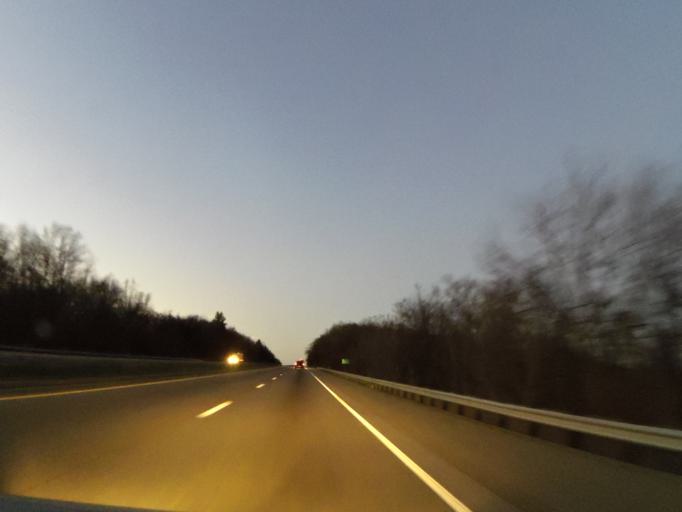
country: US
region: Tennessee
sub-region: Cocke County
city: Newport
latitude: 35.9098
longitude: -83.1856
